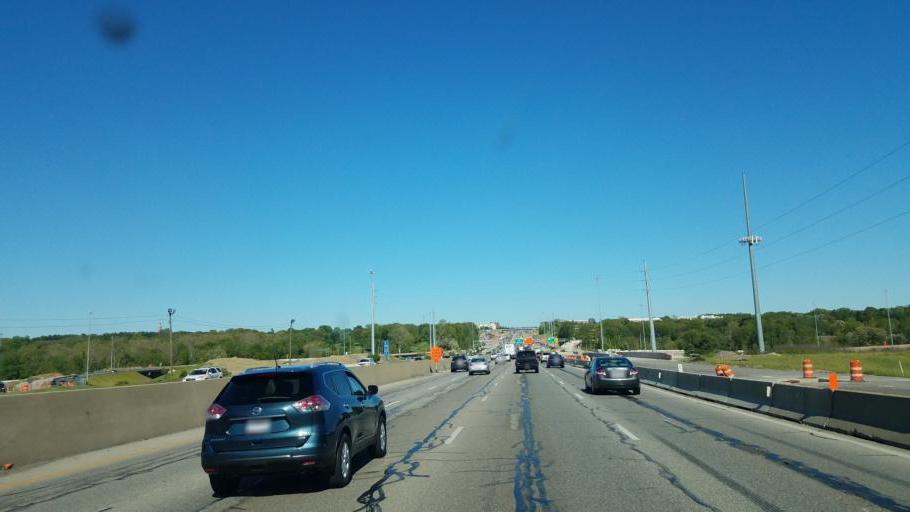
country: US
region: Ohio
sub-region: Franklin County
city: Worthington
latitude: 40.1121
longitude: -83.0396
